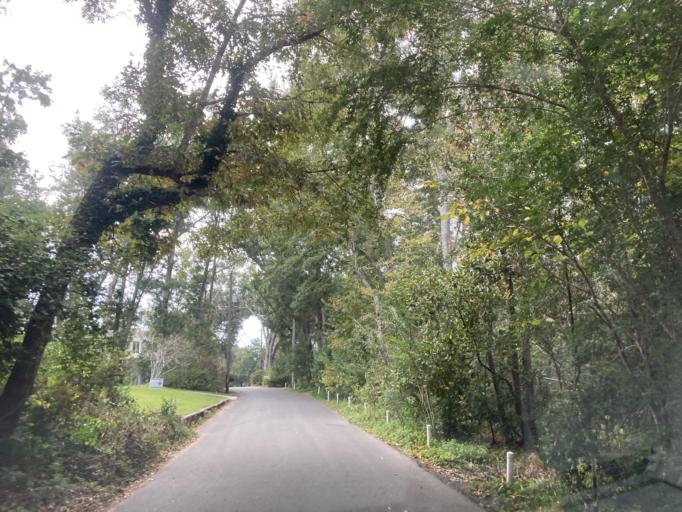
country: US
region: Mississippi
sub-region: Jackson County
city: Gulf Hills
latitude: 30.4397
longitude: -88.8411
